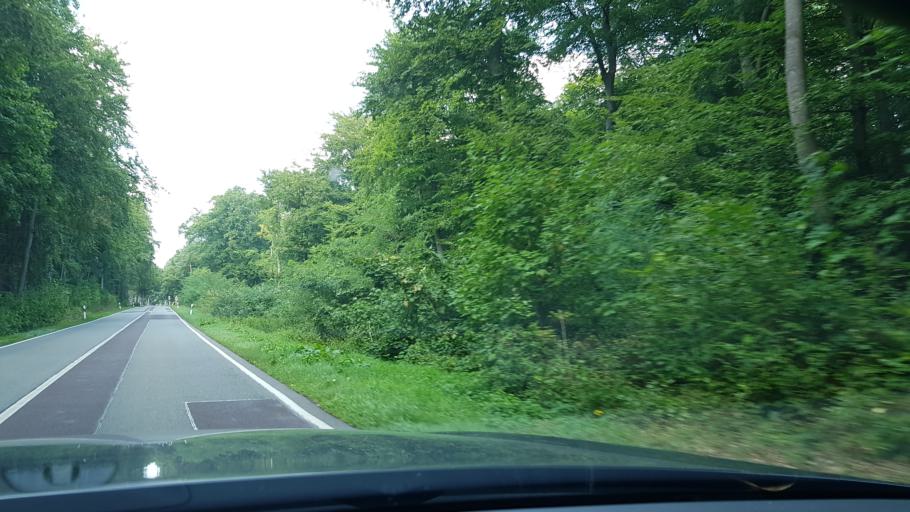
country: DE
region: Brandenburg
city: Rheinsberg
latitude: 53.0631
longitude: 12.9340
